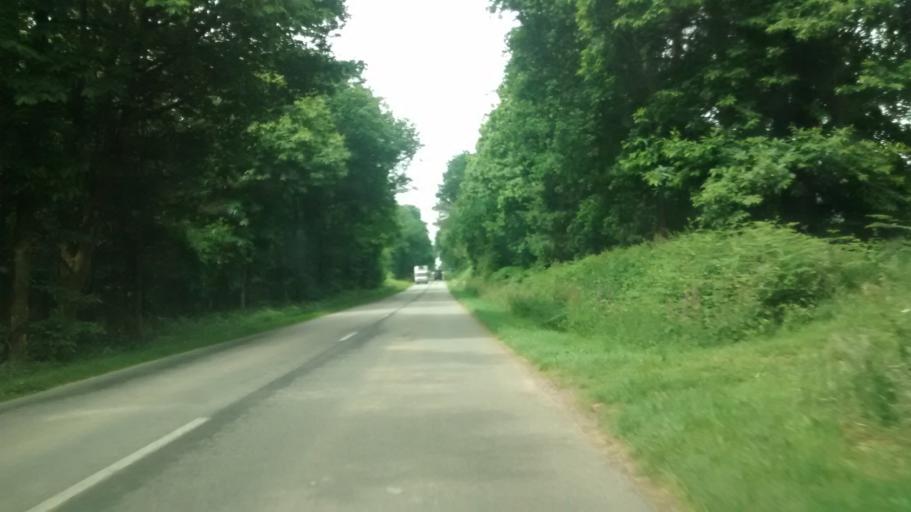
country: FR
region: Brittany
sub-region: Departement du Morbihan
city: Guer
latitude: 47.8871
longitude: -2.1754
